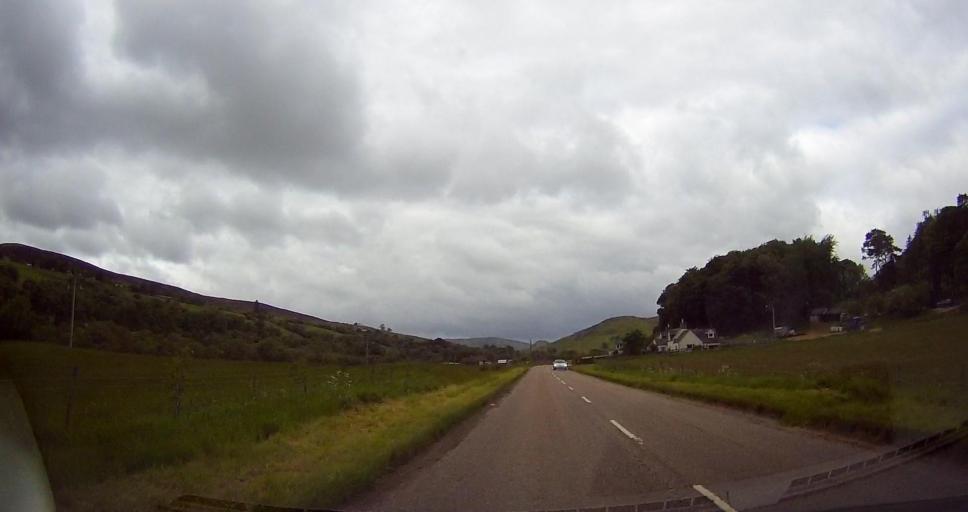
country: GB
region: Scotland
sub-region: Highland
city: Dornoch
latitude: 58.0034
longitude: -4.1966
